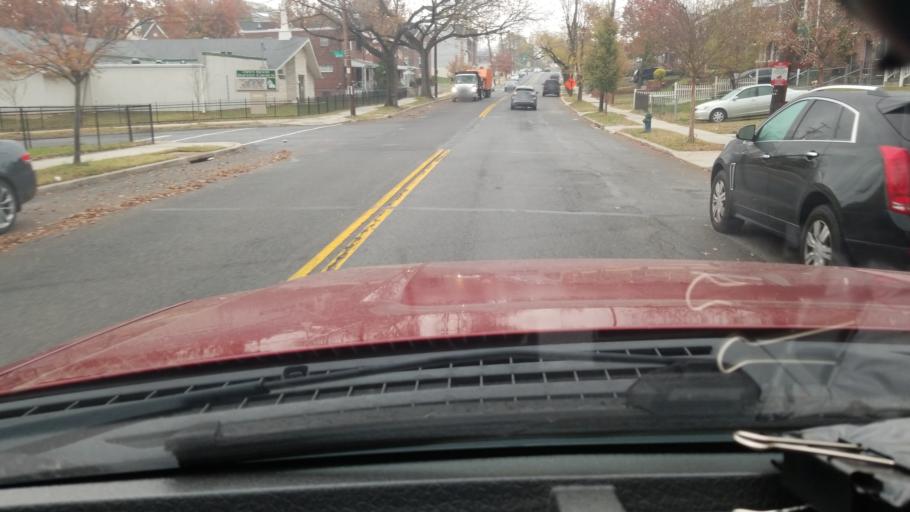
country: US
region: Maryland
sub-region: Prince George's County
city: Capitol Heights
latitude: 38.8863
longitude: -76.9213
